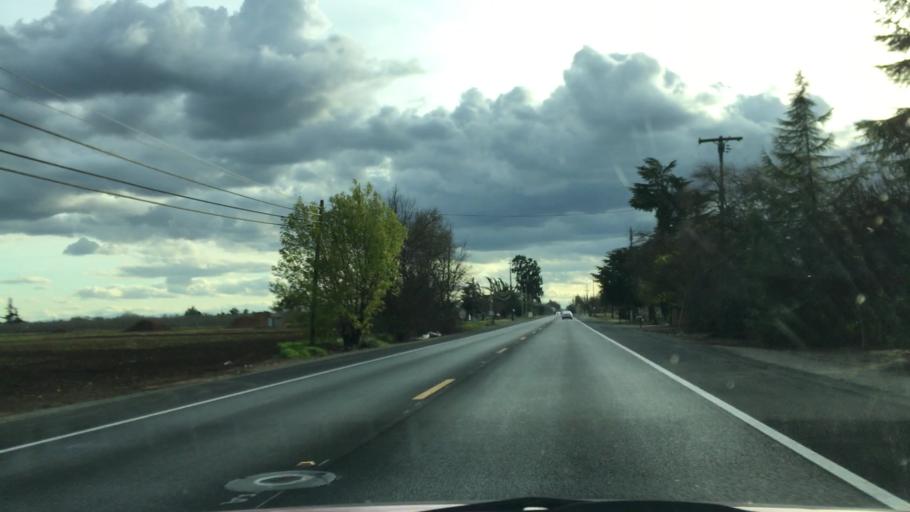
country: US
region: California
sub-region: San Joaquin County
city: Morada
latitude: 38.0123
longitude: -121.2118
